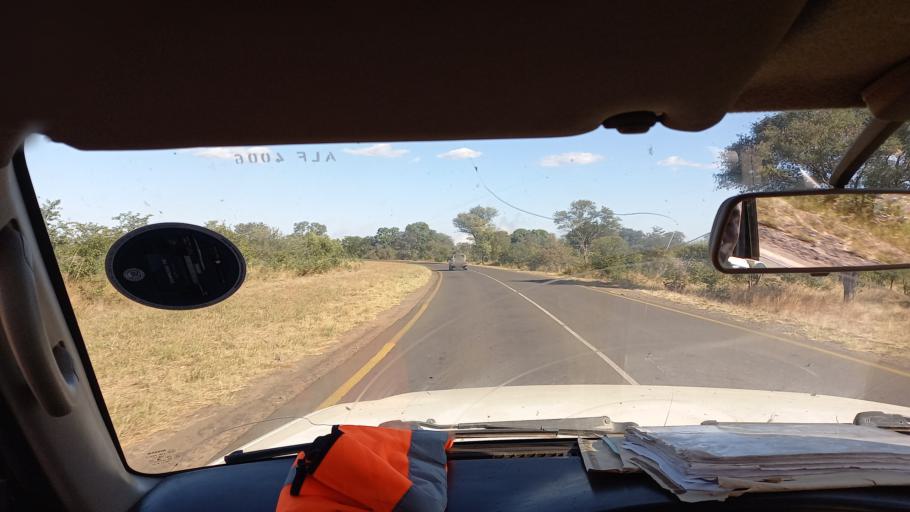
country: ZW
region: Matabeleland North
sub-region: Hwange District
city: Victoria Falls
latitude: -17.9016
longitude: 25.8554
